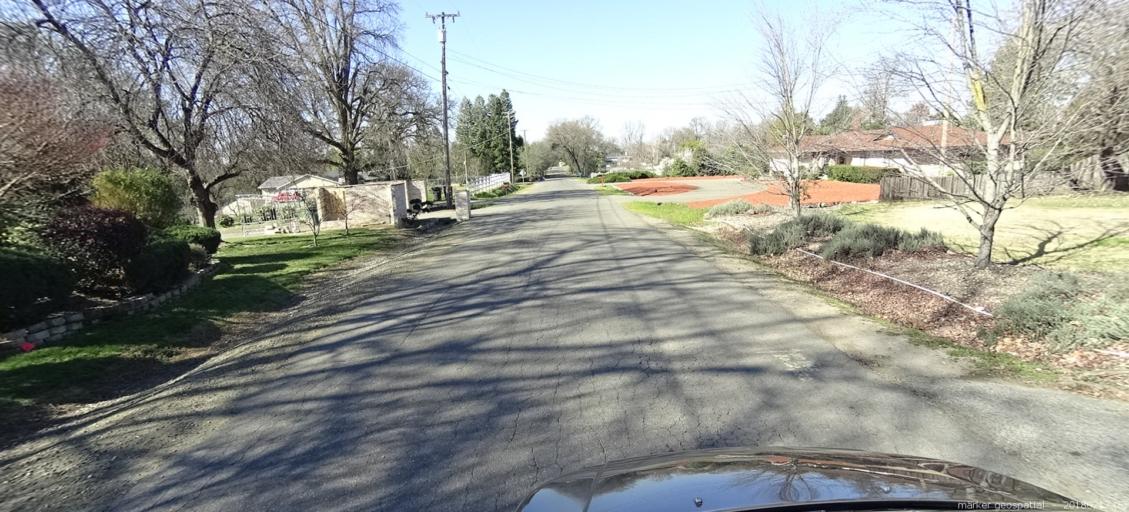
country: US
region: California
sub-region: Sacramento County
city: Orangevale
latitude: 38.7039
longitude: -121.2195
